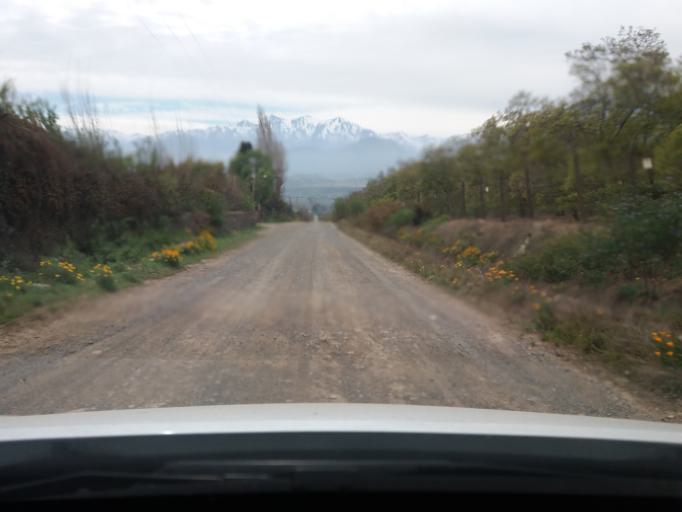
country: CL
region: Valparaiso
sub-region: Provincia de Los Andes
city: Los Andes
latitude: -32.8473
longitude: -70.5547
